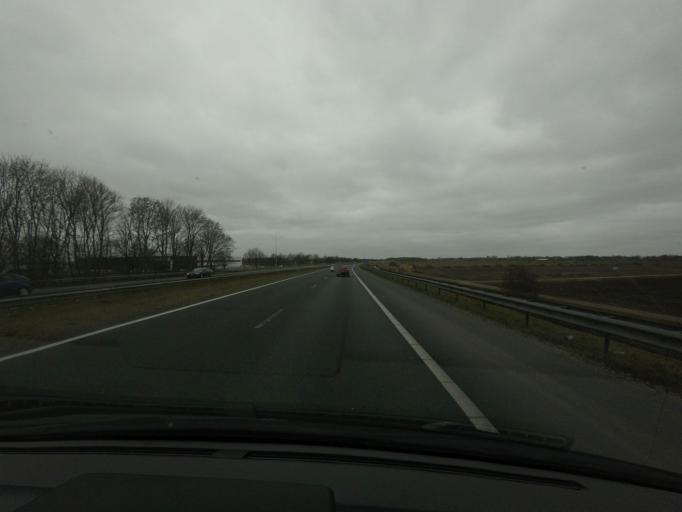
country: NL
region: Groningen
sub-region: Gemeente Hoogezand-Sappemeer
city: Hoogezand
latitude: 53.1710
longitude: 6.7518
